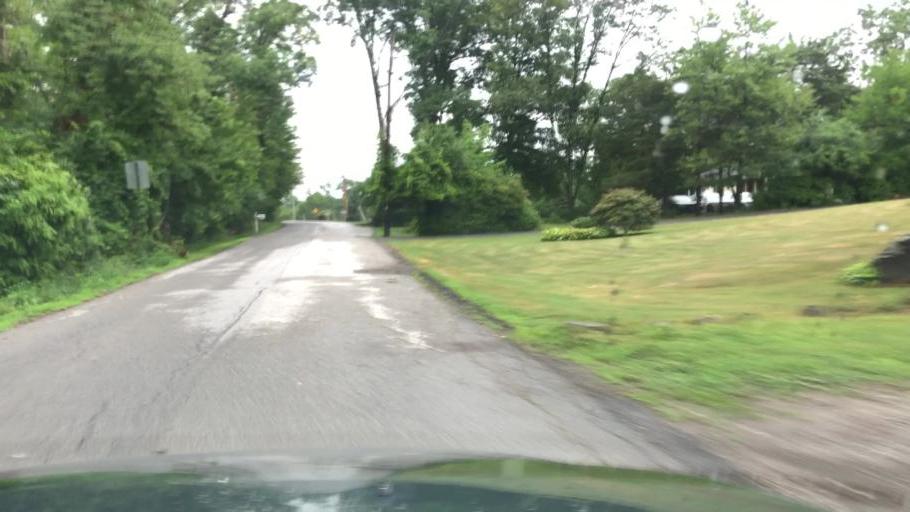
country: US
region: New York
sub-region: Dutchess County
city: Fishkill
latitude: 41.5333
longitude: -73.9351
